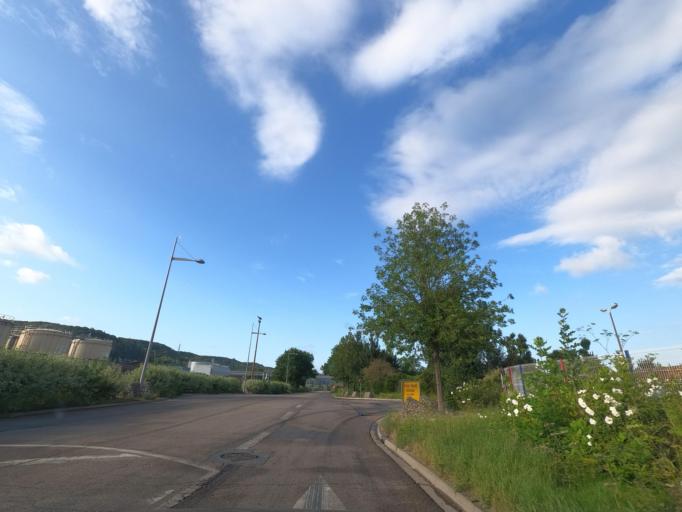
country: FR
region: Haute-Normandie
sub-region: Departement de la Seine-Maritime
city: Petit-Couronne
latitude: 49.4089
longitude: 1.0172
